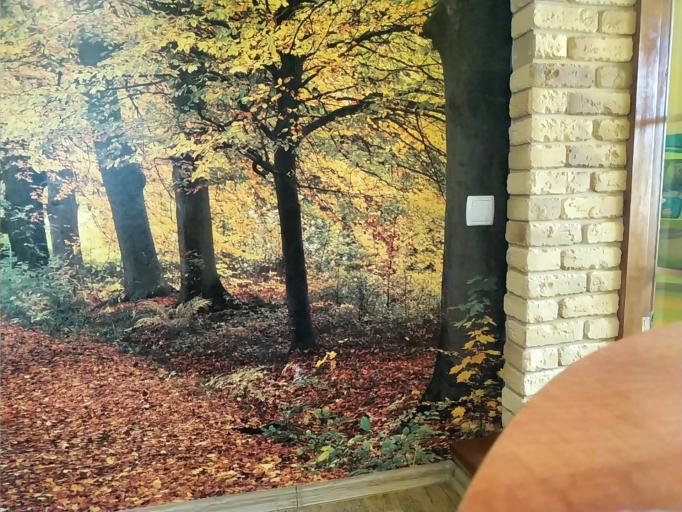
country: RU
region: Arkhangelskaya
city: Onega
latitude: 63.7099
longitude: 38.0871
